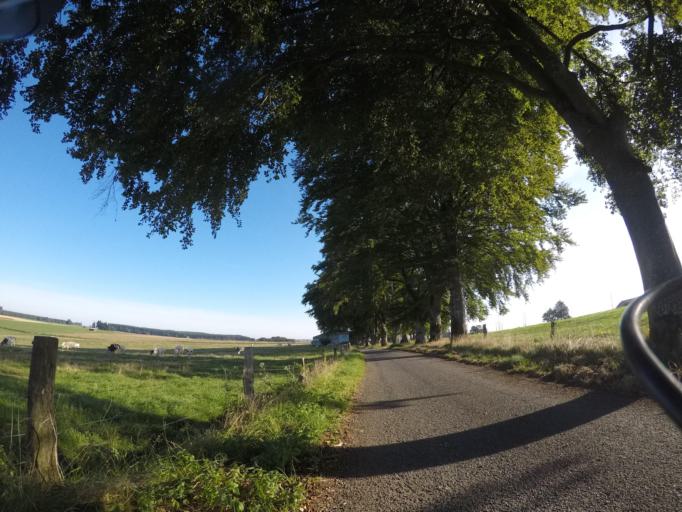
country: BE
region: Wallonia
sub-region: Province du Luxembourg
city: Bastogne
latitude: 49.9642
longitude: 5.7129
